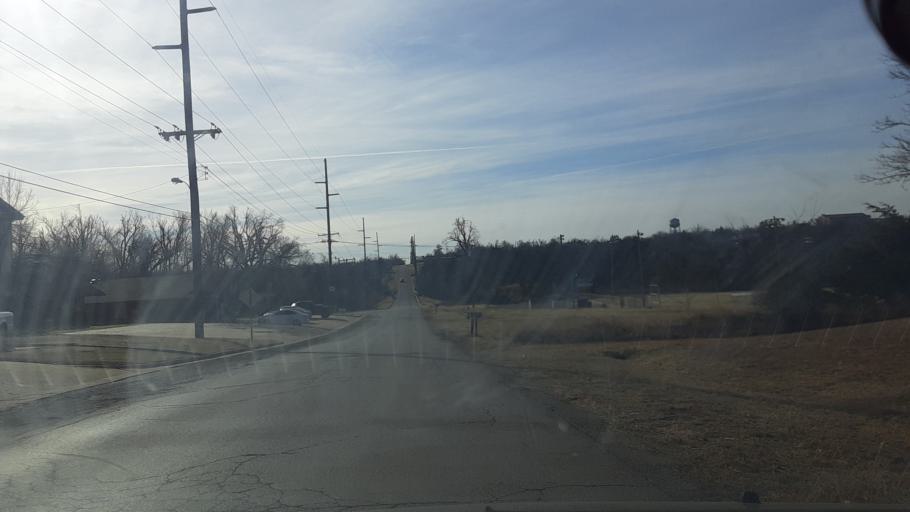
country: US
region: Oklahoma
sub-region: Logan County
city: Guthrie
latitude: 35.8863
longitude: -97.4076
